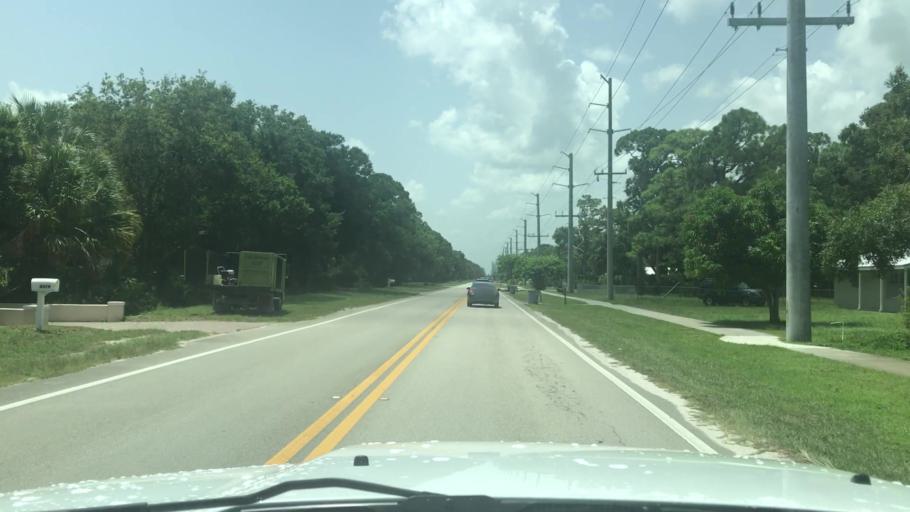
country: US
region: Florida
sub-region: Indian River County
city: Vero Beach South
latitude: 27.6238
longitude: -80.4189
